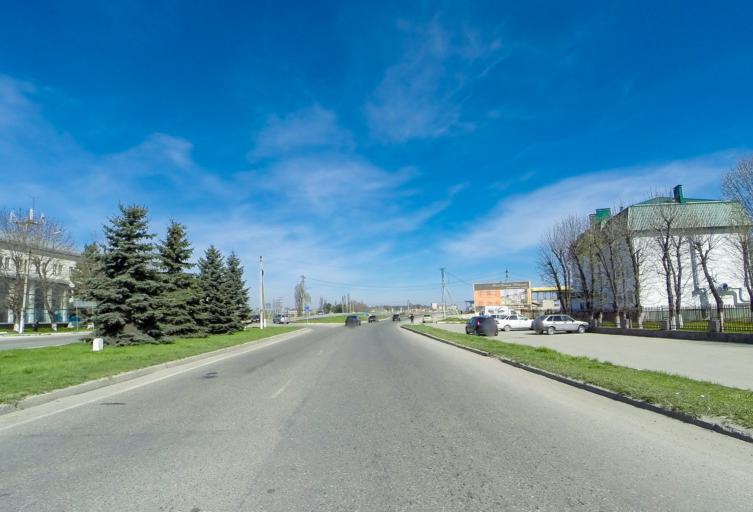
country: RU
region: Kabardino-Balkariya
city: Chegem Vtoroy
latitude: 43.5728
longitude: 43.5854
